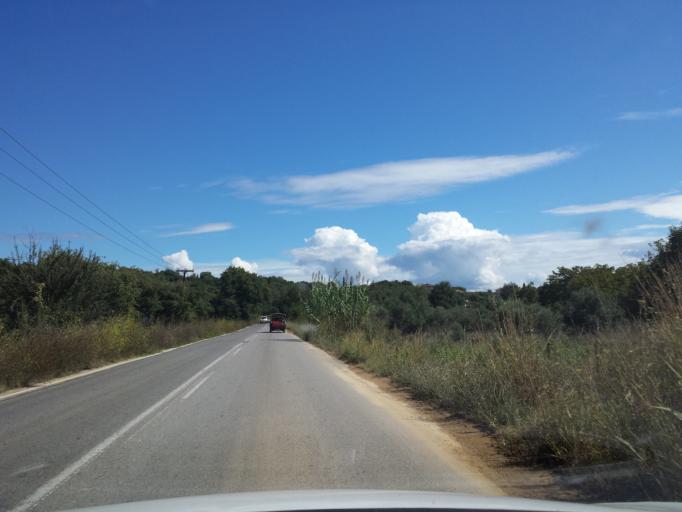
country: GR
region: Peloponnese
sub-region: Nomos Messinias
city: Vlakhopoulon
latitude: 36.9982
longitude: 21.8408
